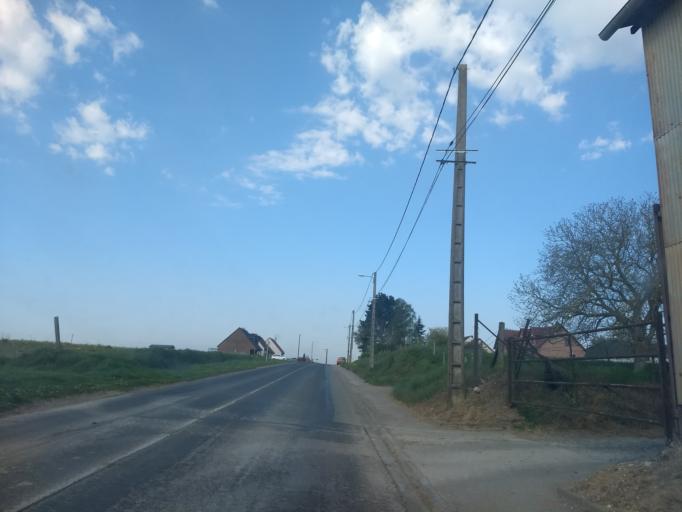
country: FR
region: Picardie
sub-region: Departement de la Somme
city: Corbie
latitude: 50.0100
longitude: 2.5127
